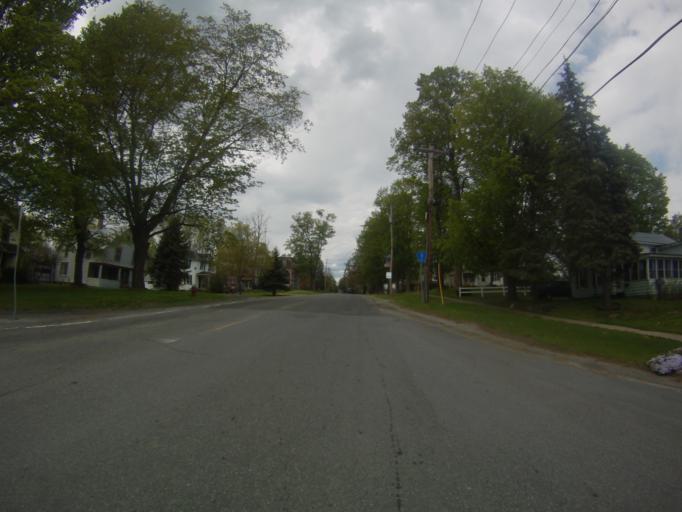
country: US
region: New York
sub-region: Essex County
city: Port Henry
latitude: 44.0462
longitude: -73.5053
